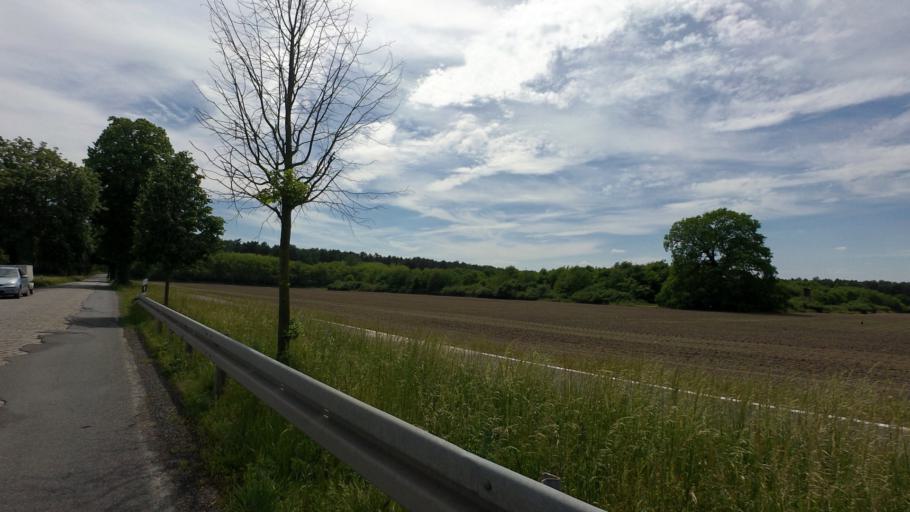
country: DE
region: Brandenburg
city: Rangsdorf
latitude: 52.3115
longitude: 13.3855
